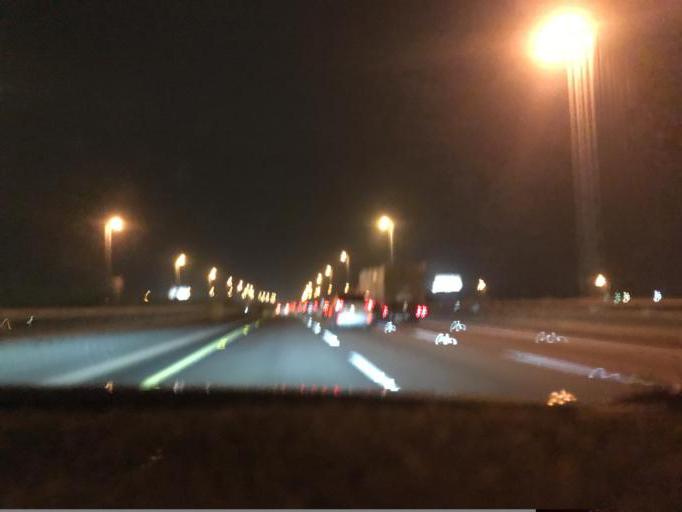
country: TW
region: Taiwan
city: Fengyuan
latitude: 24.3961
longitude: 120.6693
